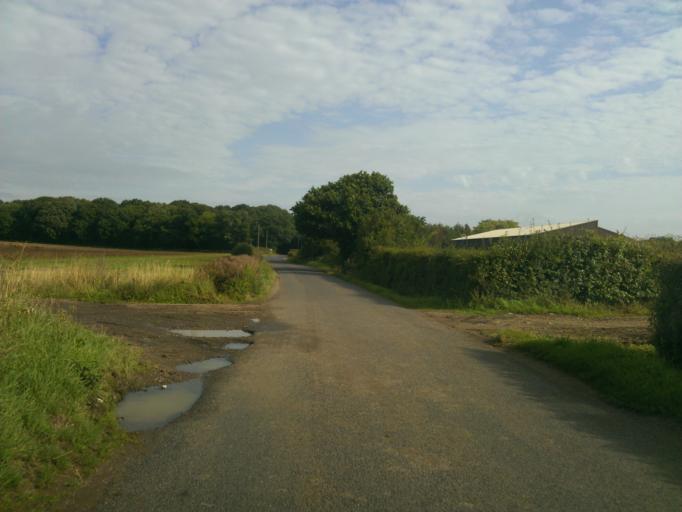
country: GB
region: England
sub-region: Essex
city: Saint Osyth
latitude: 51.8303
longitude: 1.1031
